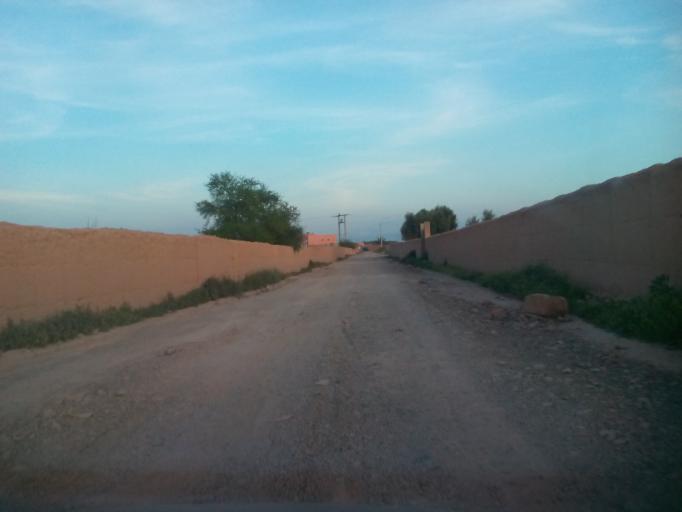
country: MA
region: Marrakech-Tensift-Al Haouz
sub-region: Marrakech
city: Marrakesh
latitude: 31.6267
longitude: -8.2859
